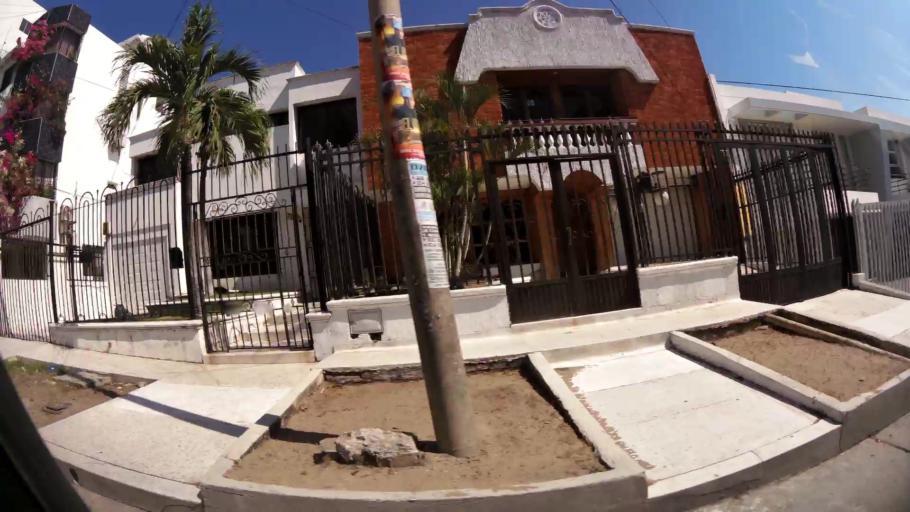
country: CO
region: Atlantico
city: Barranquilla
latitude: 11.0125
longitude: -74.8224
